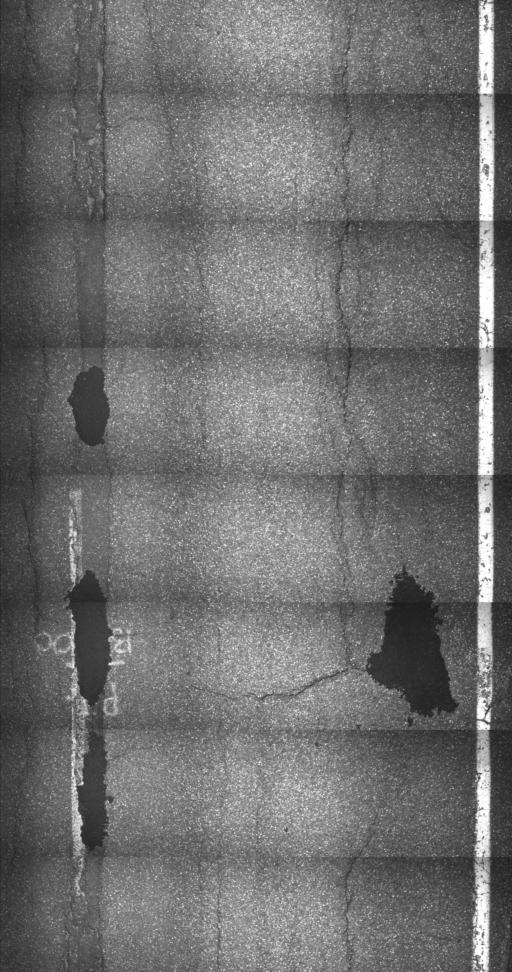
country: US
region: Vermont
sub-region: Orange County
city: Randolph
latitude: 43.9540
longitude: -72.6498
